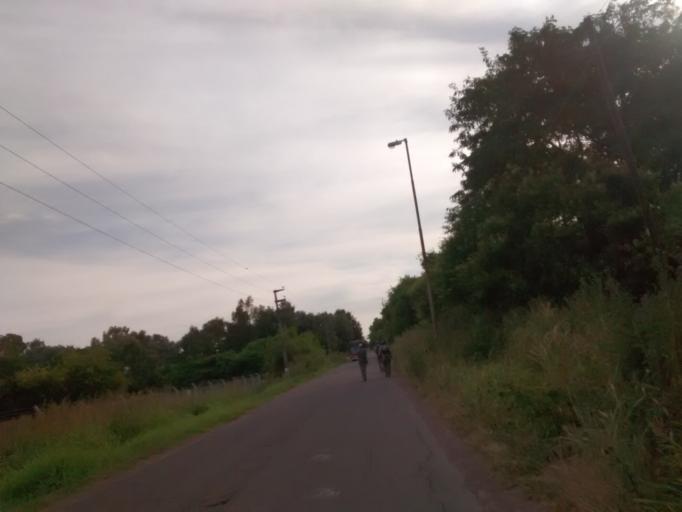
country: AR
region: Buenos Aires
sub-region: Partido de La Plata
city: La Plata
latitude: -34.8444
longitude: -58.0952
